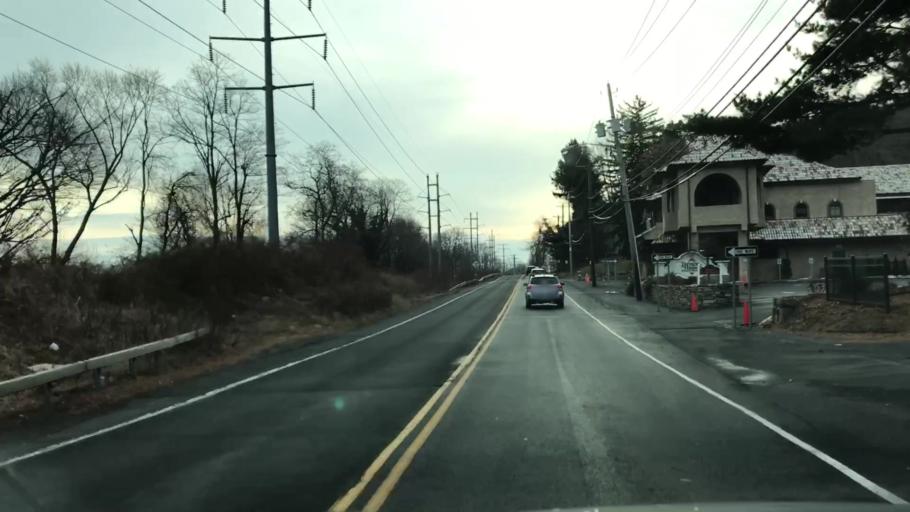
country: US
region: New York
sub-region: Rockland County
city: Haverstraw
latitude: 41.1932
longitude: -73.9669
